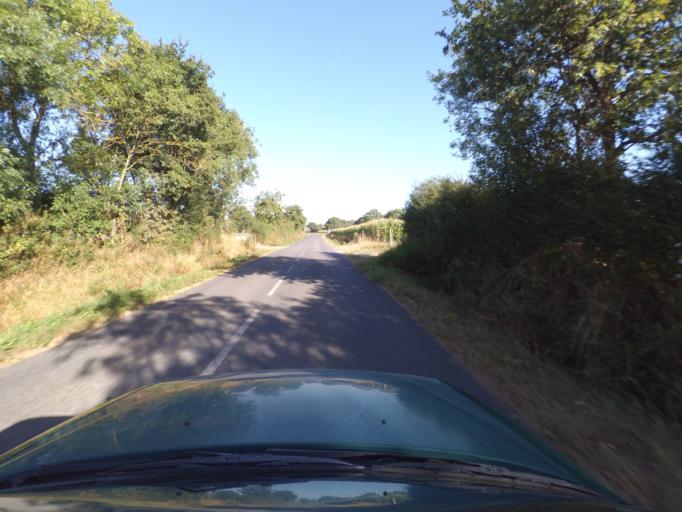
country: FR
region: Pays de la Loire
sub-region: Departement de la Loire-Atlantique
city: Le Bignon
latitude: 47.1029
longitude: -1.5045
